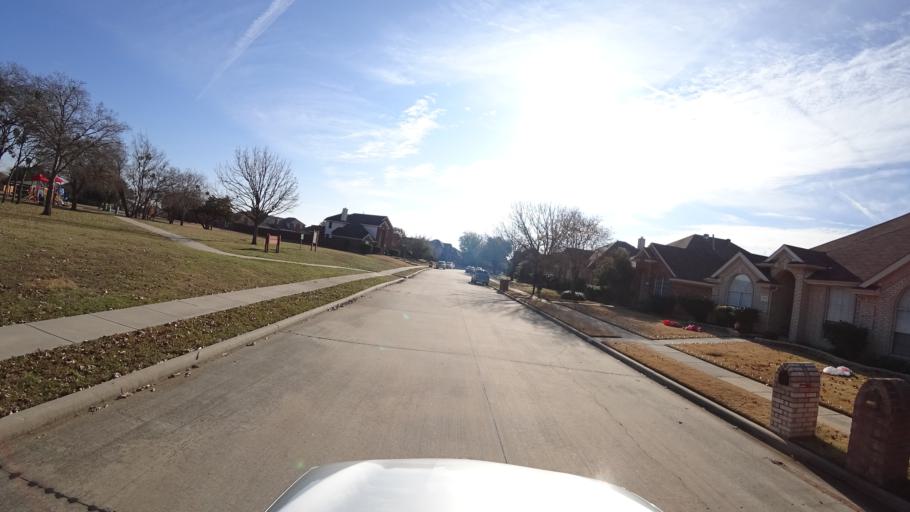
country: US
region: Texas
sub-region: Denton County
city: Lewisville
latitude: 33.0599
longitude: -97.0249
